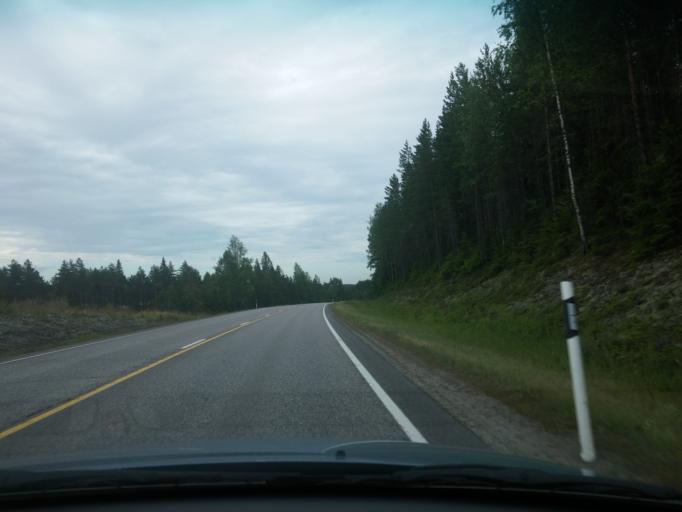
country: FI
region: Haeme
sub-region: Riihimaeki
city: Loppi
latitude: 60.7368
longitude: 24.3777
